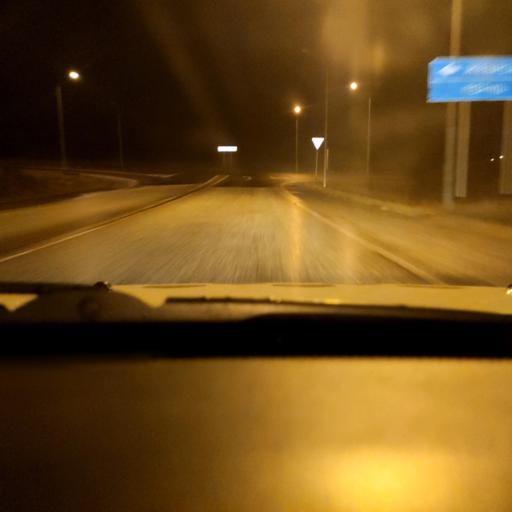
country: RU
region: Perm
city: Ferma
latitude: 57.9510
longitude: 56.3925
